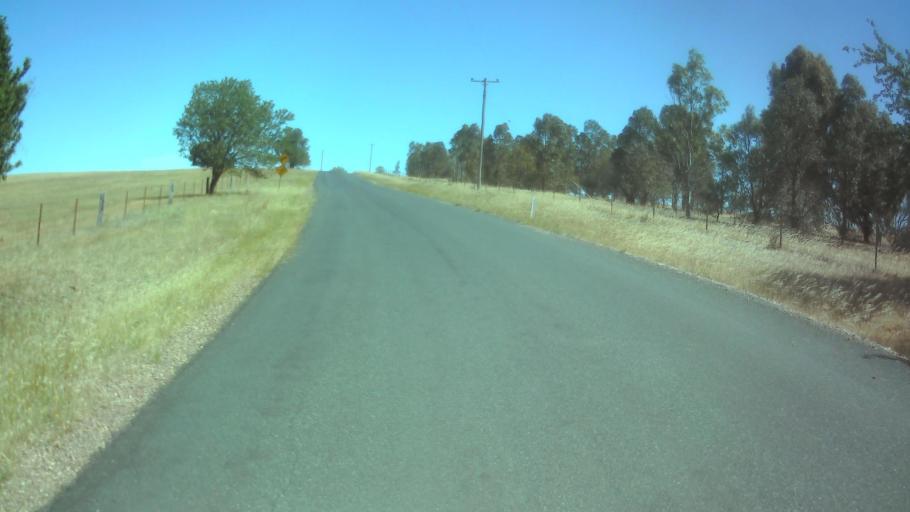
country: AU
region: New South Wales
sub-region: Weddin
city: Grenfell
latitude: -33.9632
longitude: 148.4056
